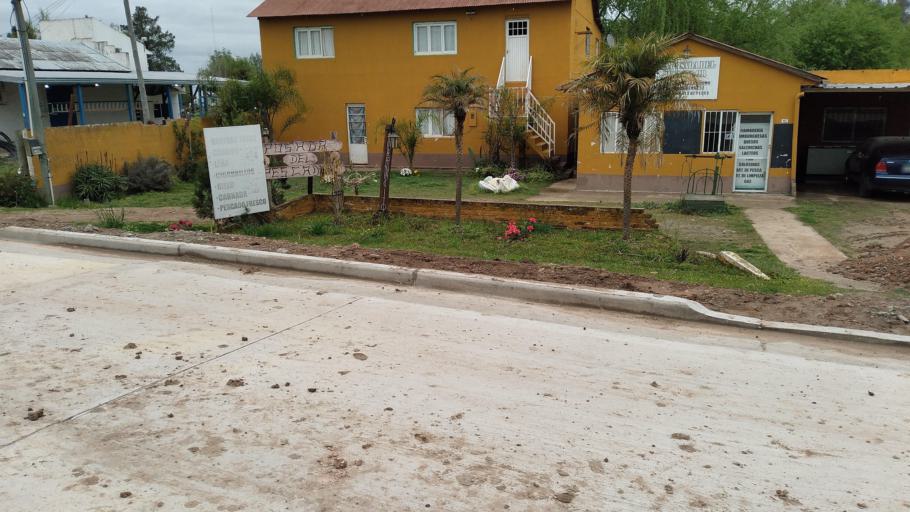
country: AR
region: Entre Rios
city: Villa Paranacito
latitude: -33.7158
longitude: -58.6641
